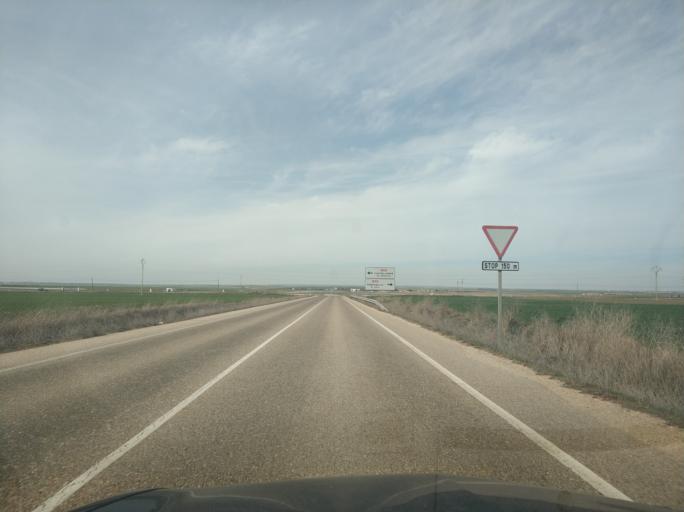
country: ES
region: Castille and Leon
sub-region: Provincia de Salamanca
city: Castellanos de Moriscos
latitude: 41.0305
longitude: -5.5770
